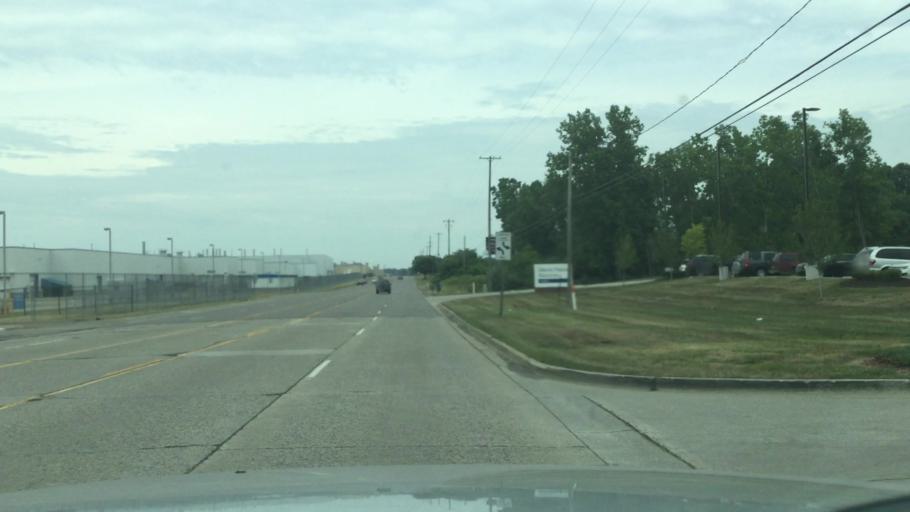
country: US
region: Michigan
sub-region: Genesee County
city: Flint
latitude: 42.9747
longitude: -83.7128
